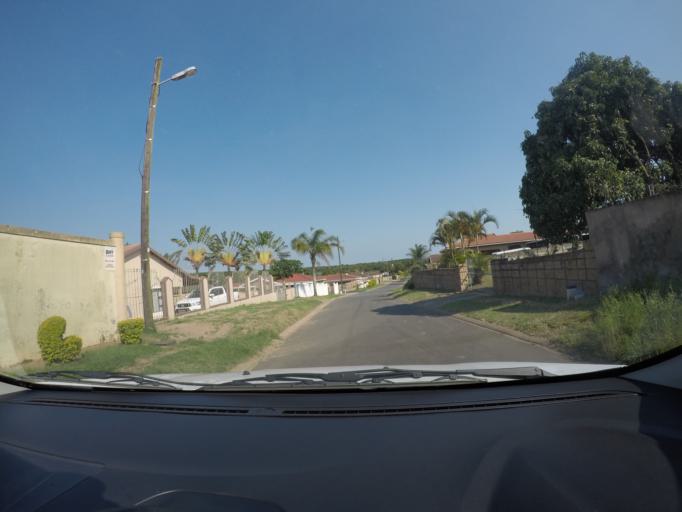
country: ZA
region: KwaZulu-Natal
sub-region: uThungulu District Municipality
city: Richards Bay
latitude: -28.7168
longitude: 32.0432
